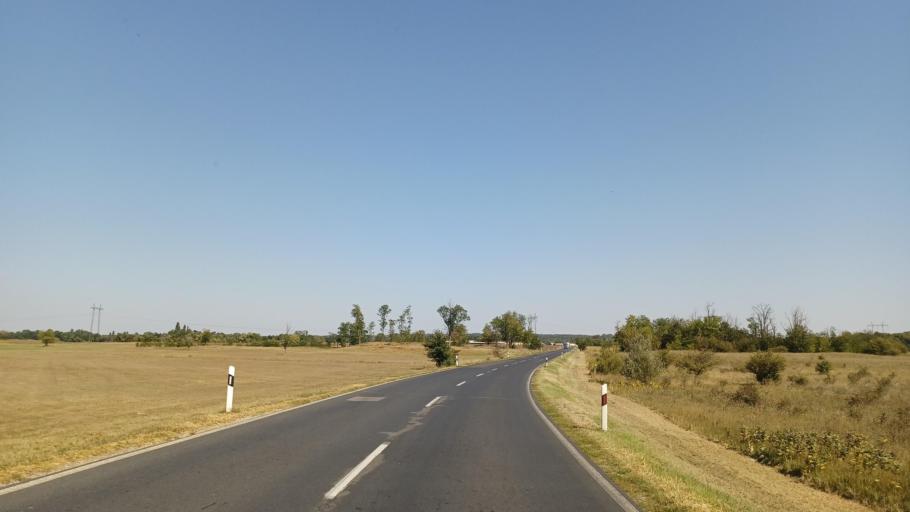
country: HU
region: Tolna
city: Nagydorog
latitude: 46.6608
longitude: 18.6537
